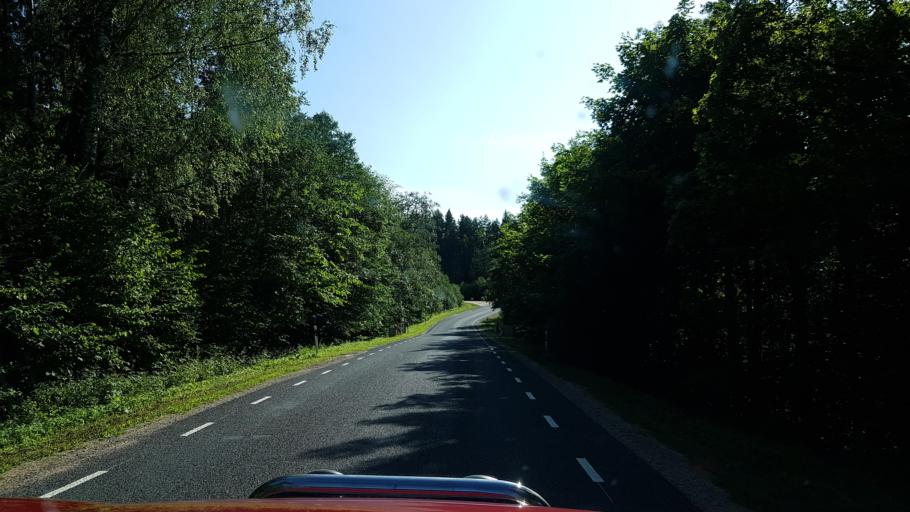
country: LV
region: Aloja
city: Staicele
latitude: 58.0925
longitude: 24.6819
